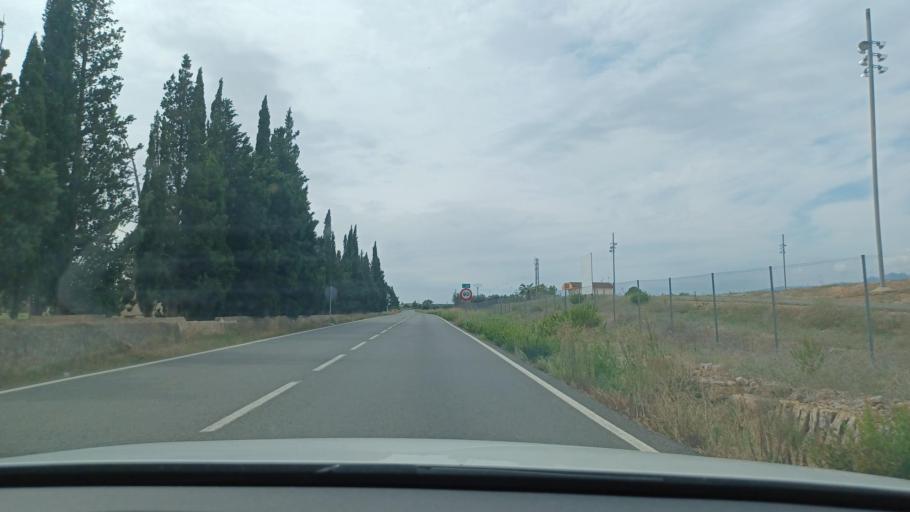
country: ES
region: Catalonia
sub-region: Provincia de Tarragona
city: Tortosa
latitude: 40.7706
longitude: 0.5113
